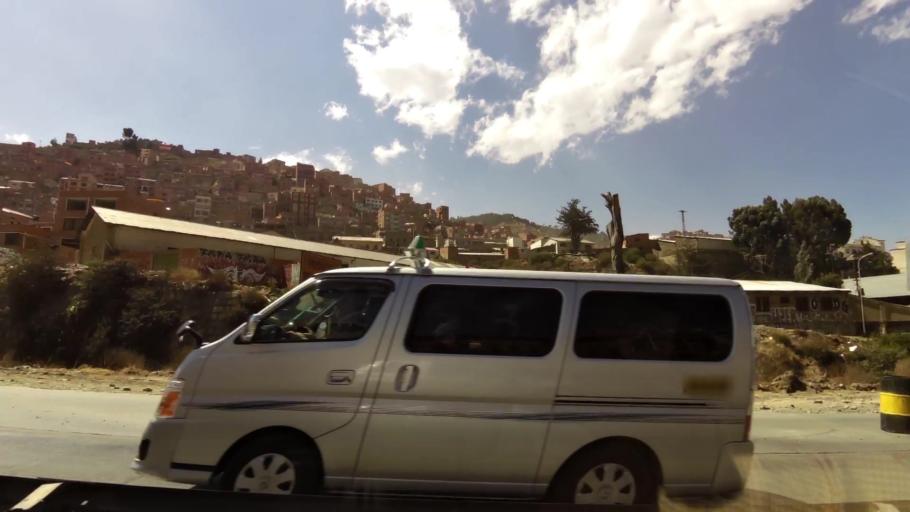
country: BO
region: La Paz
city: La Paz
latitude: -16.4831
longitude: -68.1477
